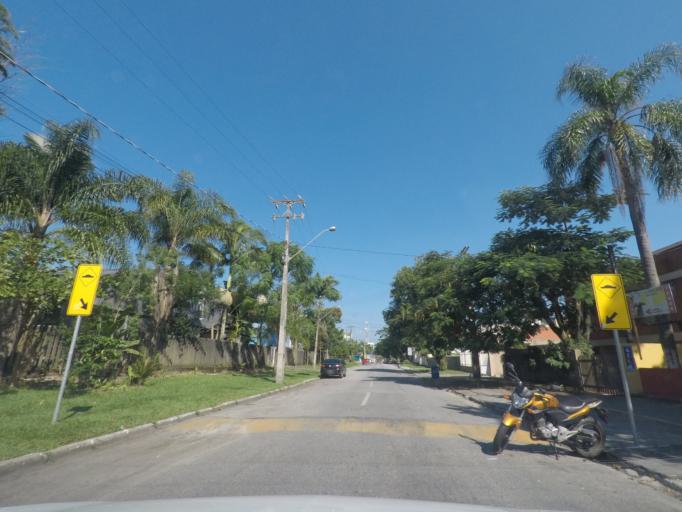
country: BR
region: Parana
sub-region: Guaratuba
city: Guaratuba
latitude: -25.8344
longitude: -48.5394
